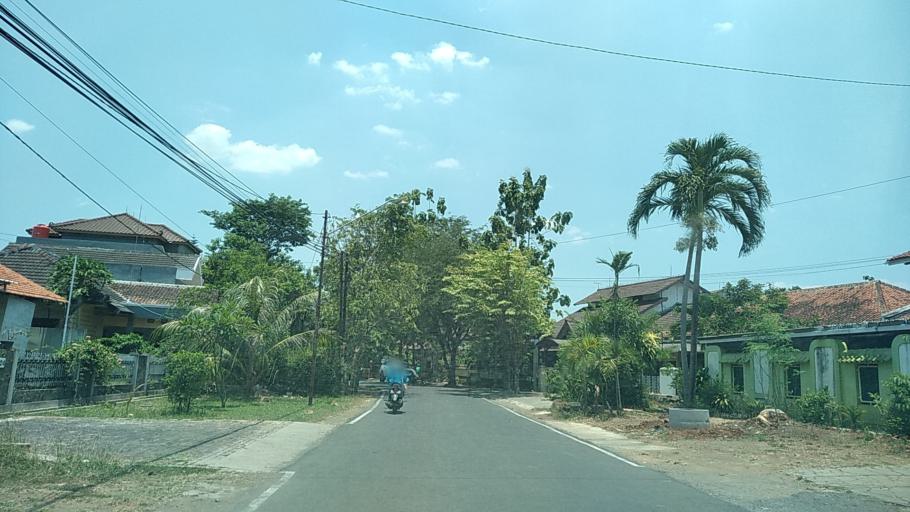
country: ID
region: Central Java
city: Ungaran
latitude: -7.0728
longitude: 110.4252
